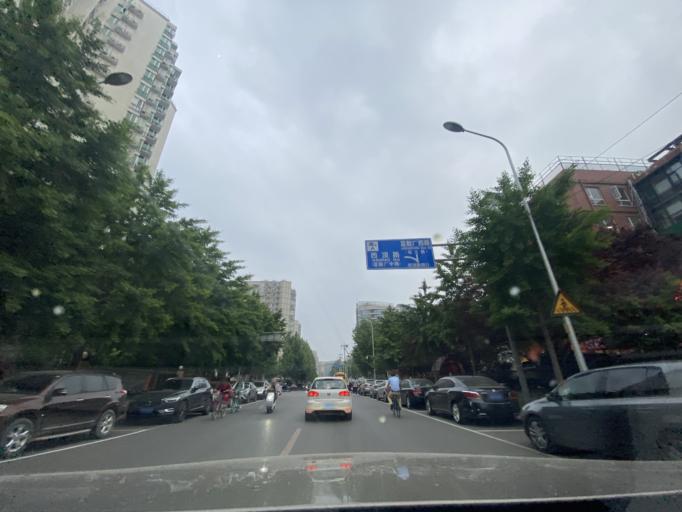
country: CN
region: Beijing
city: Sijiqing
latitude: 39.9587
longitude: 116.2744
